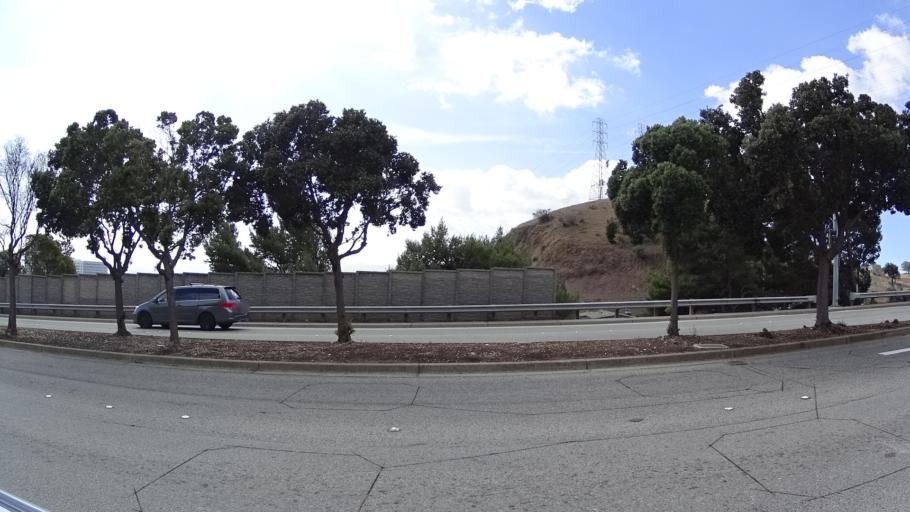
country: US
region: California
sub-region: San Mateo County
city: South San Francisco
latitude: 37.6659
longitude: -122.4049
